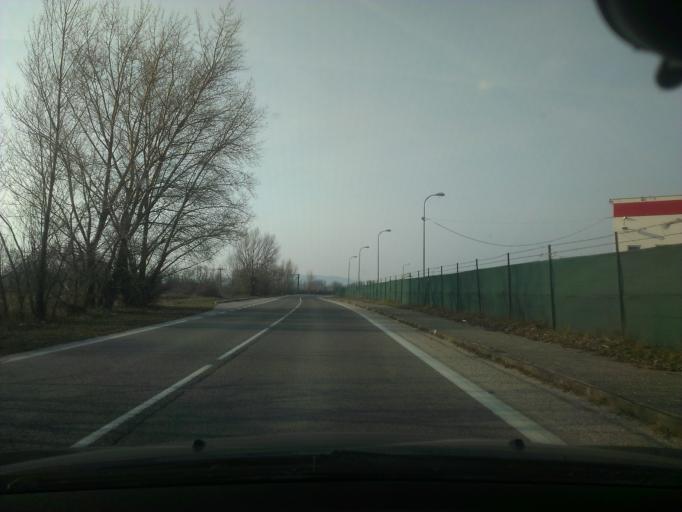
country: SK
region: Trnavsky
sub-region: Okres Trnava
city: Piestany
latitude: 48.6664
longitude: 17.8755
